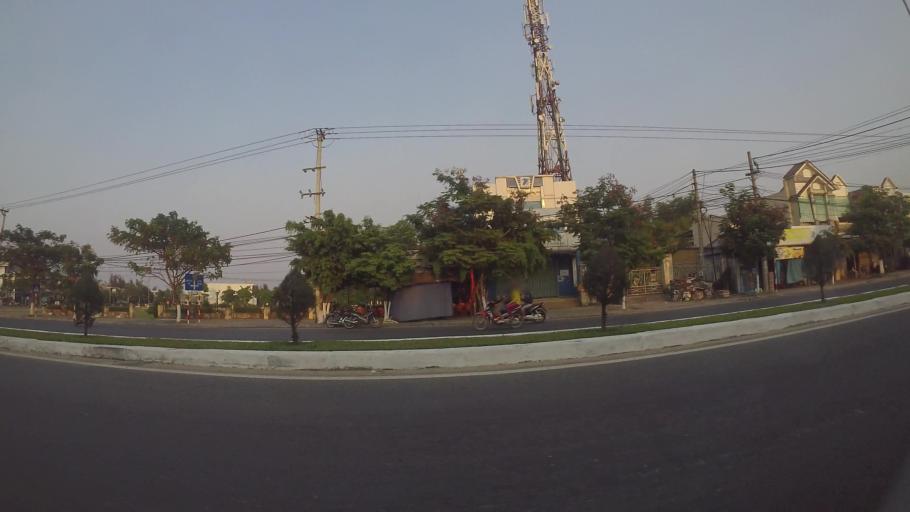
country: VN
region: Da Nang
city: Ngu Hanh Son
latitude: 15.9554
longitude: 108.2548
